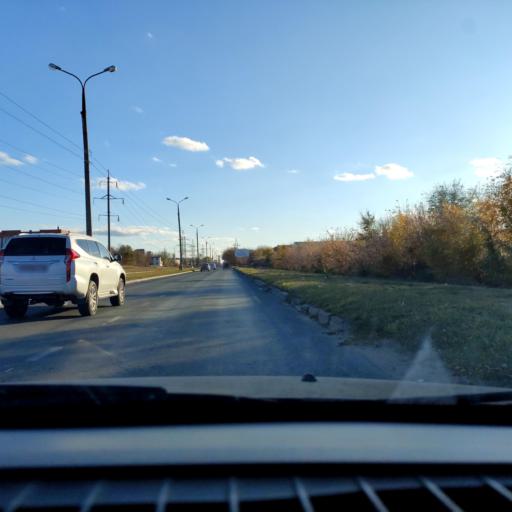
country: RU
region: Samara
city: Tol'yatti
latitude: 53.5575
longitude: 49.3194
